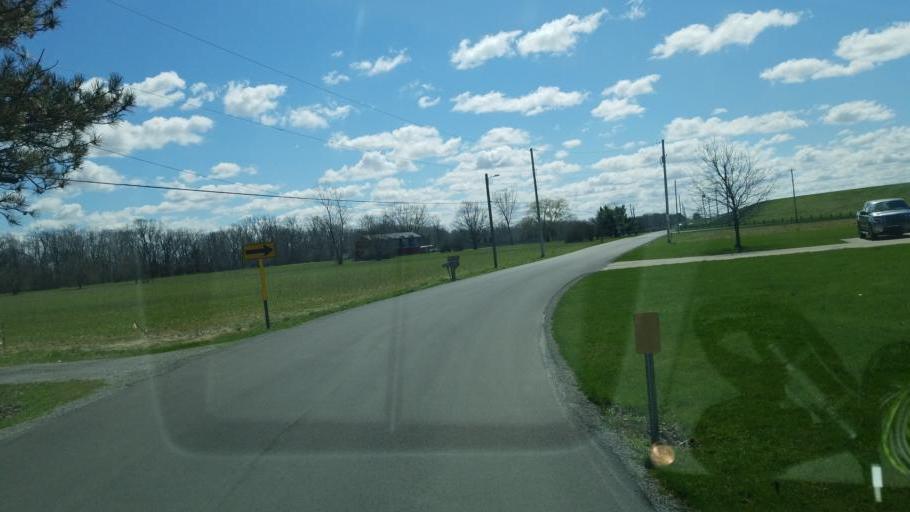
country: US
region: Ohio
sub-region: Hancock County
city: Findlay
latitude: 41.0289
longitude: -83.5595
